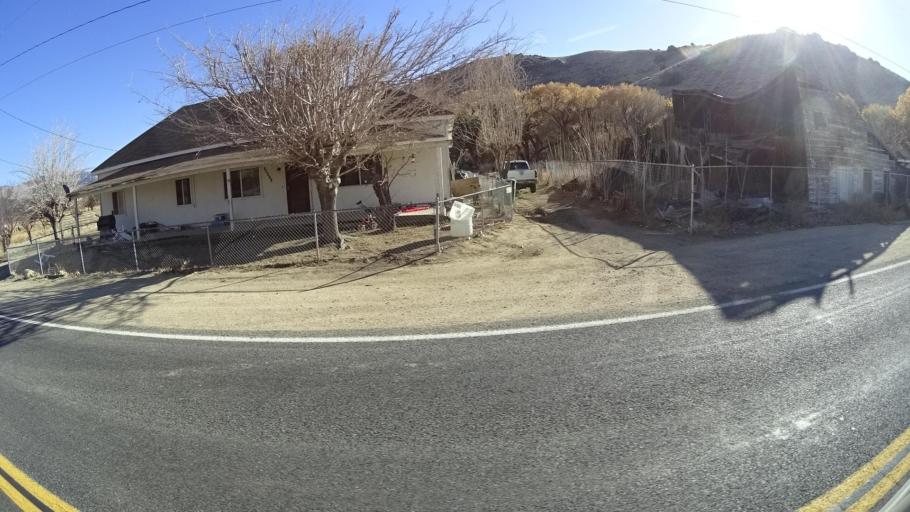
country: US
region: California
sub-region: Kern County
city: Weldon
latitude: 35.6644
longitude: -118.3021
